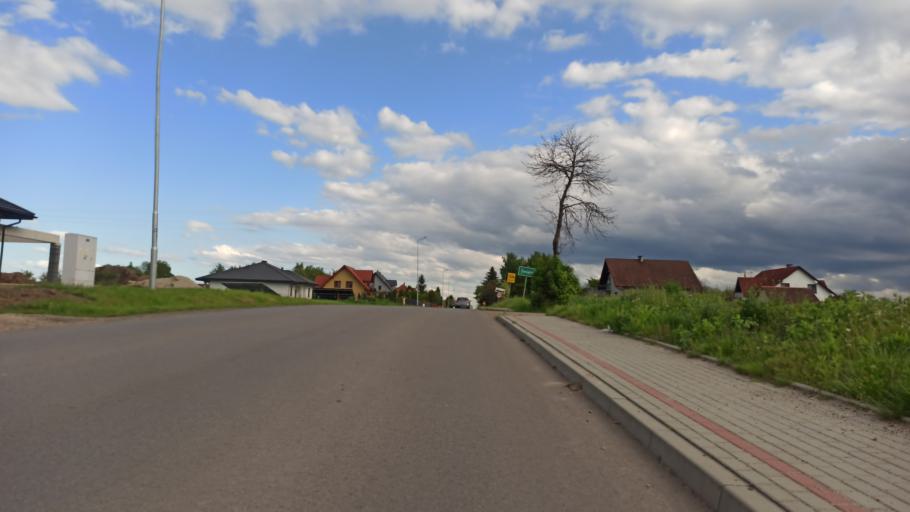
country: PL
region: Subcarpathian Voivodeship
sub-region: Powiat jaroslawski
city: Radymno
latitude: 49.9315
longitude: 22.8417
